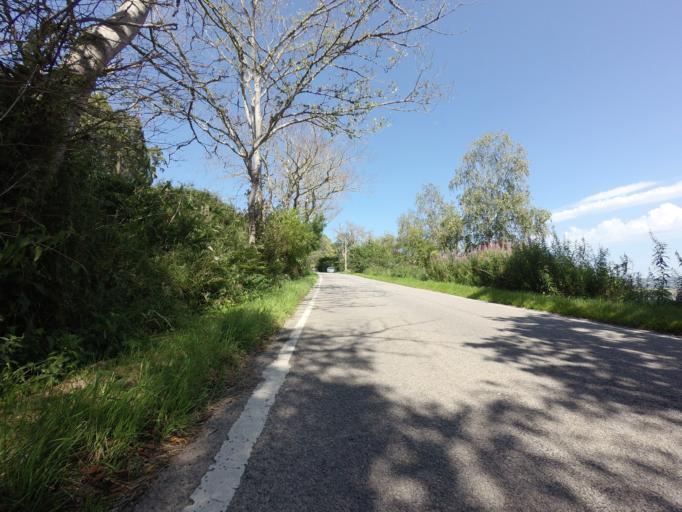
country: GB
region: Scotland
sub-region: Highland
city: Dingwall
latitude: 57.6132
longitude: -4.4135
